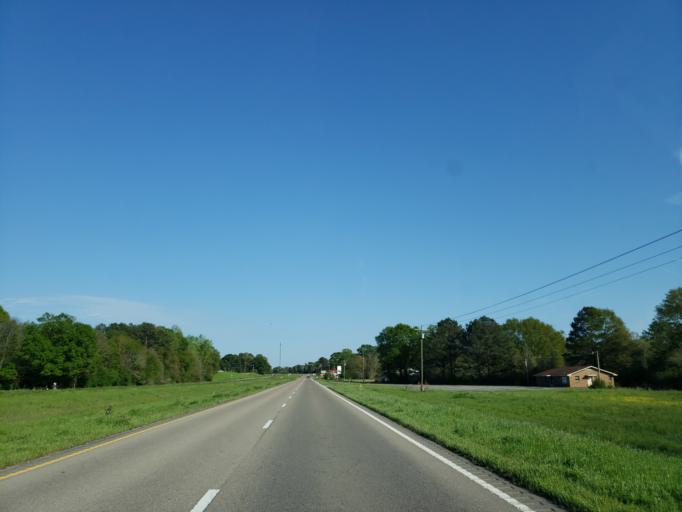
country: US
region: Mississippi
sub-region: Jones County
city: Ellisville
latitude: 31.6790
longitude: -89.3048
